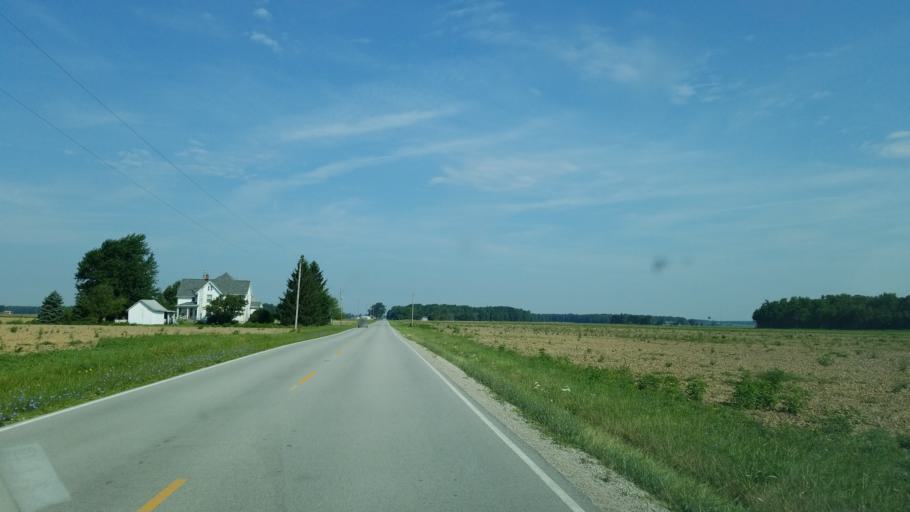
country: US
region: Ohio
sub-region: Huron County
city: Willard
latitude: 41.0156
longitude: -82.8583
